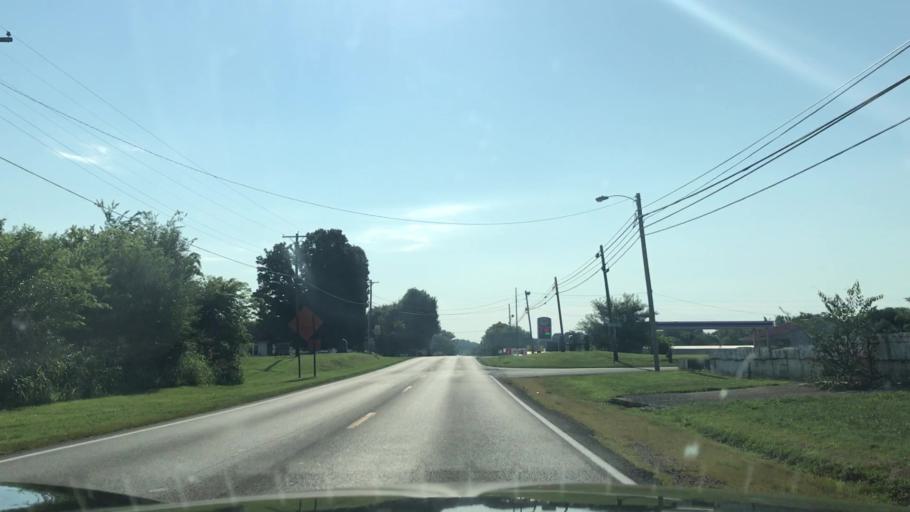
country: US
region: Kentucky
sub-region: Hart County
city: Horse Cave
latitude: 37.1781
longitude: -85.8910
